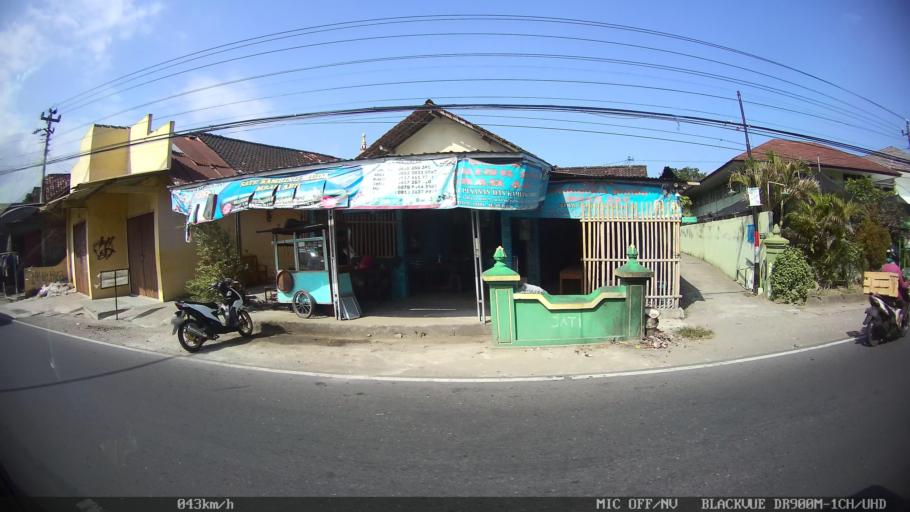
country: ID
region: Daerah Istimewa Yogyakarta
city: Sewon
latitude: -7.8638
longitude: 110.3894
